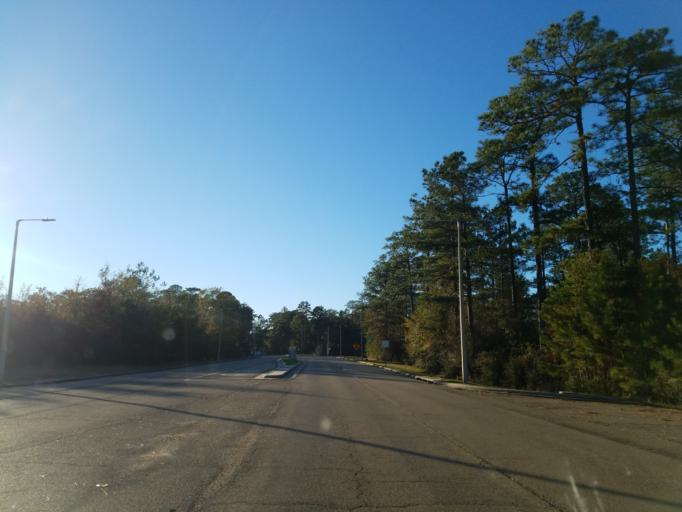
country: US
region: Mississippi
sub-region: Lamar County
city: Arnold Line
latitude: 31.3538
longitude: -89.3708
